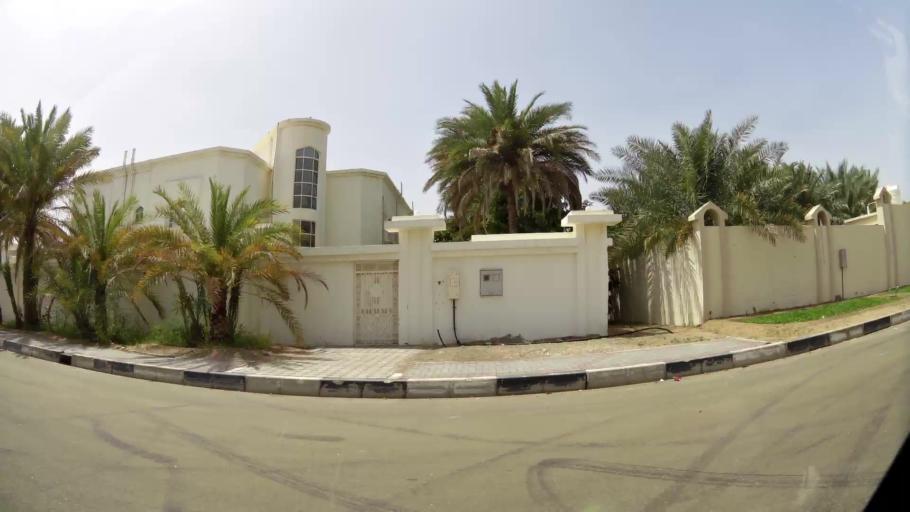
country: AE
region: Abu Dhabi
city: Al Ain
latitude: 24.1438
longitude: 55.6441
